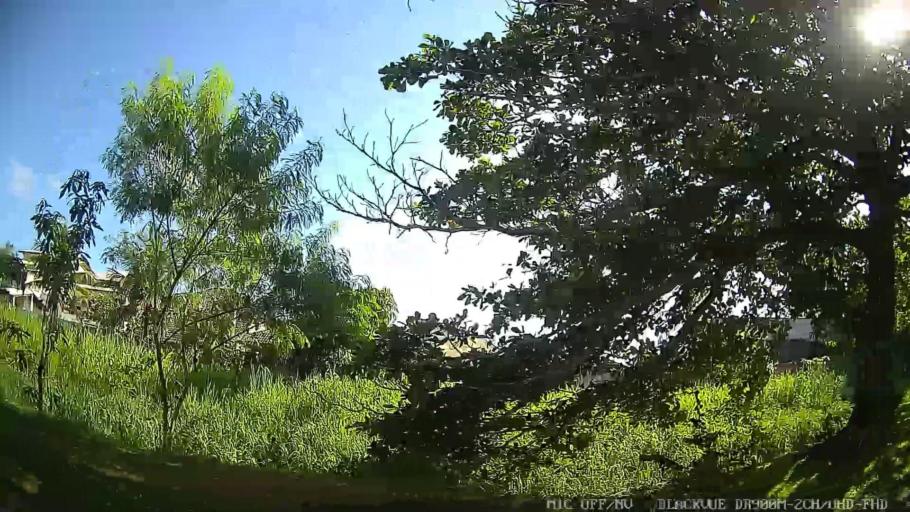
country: BR
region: Sao Paulo
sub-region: Peruibe
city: Peruibe
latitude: -24.2892
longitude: -46.9566
